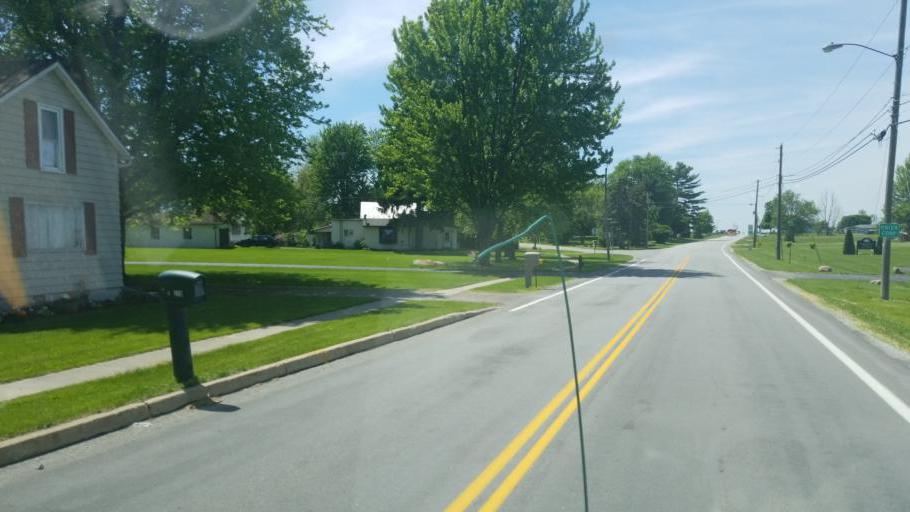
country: US
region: Ohio
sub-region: Huron County
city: Willard
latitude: 41.0661
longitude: -82.8917
